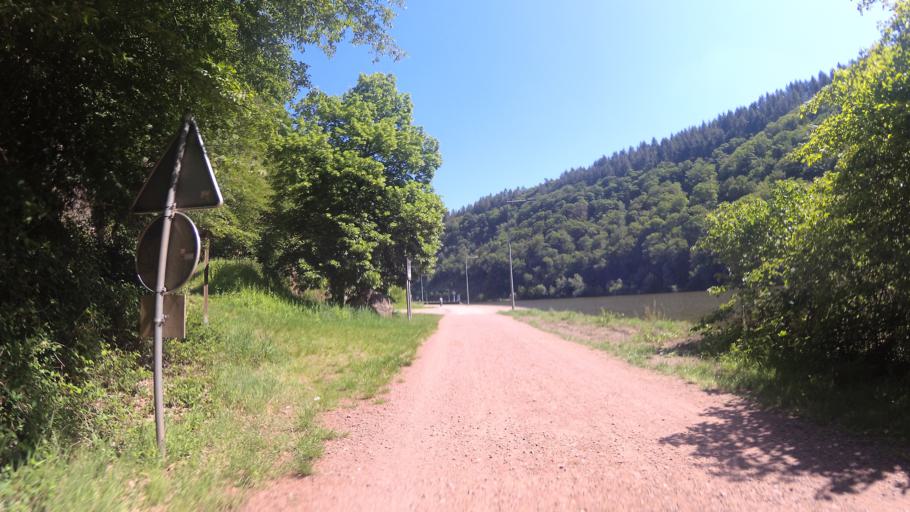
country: DE
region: Saarland
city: Mettlach
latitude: 49.4924
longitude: 6.5730
